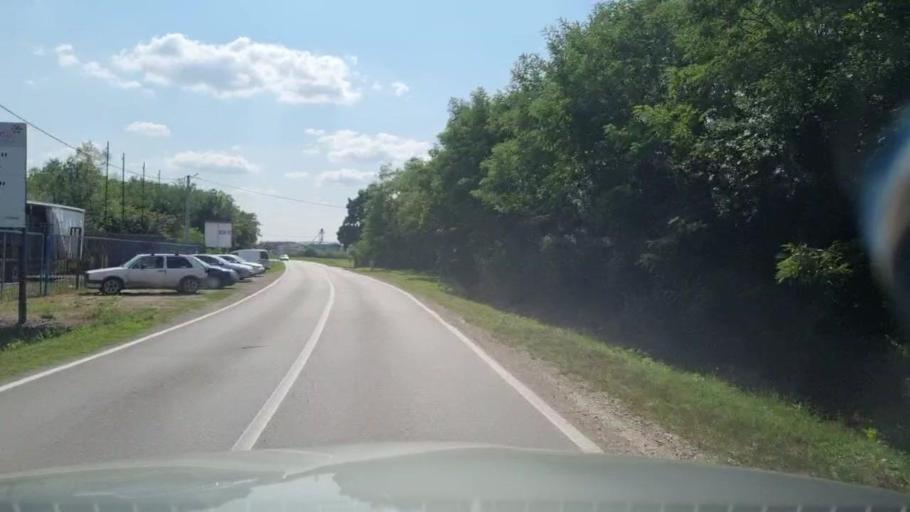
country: BA
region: Federation of Bosnia and Herzegovina
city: Odzak
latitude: 45.0269
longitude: 18.3430
